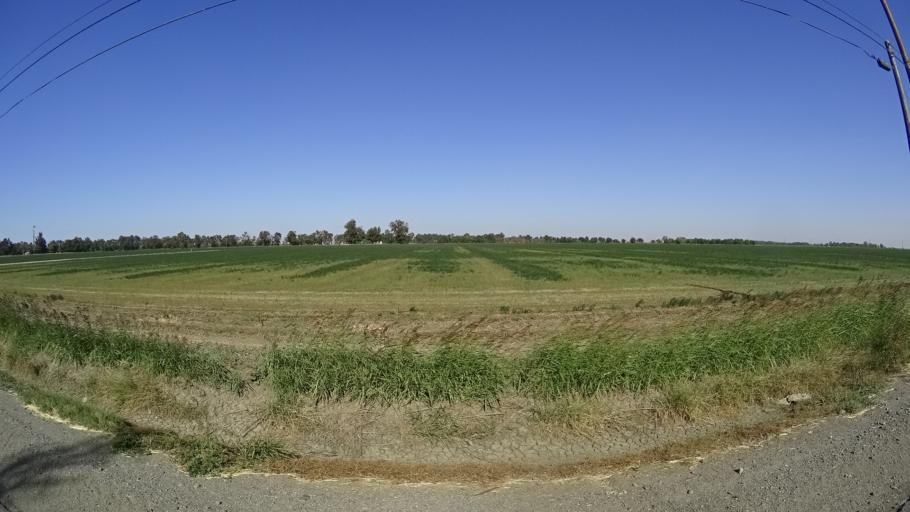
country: US
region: California
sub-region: Yolo County
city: Woodland
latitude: 38.6188
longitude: -121.7374
